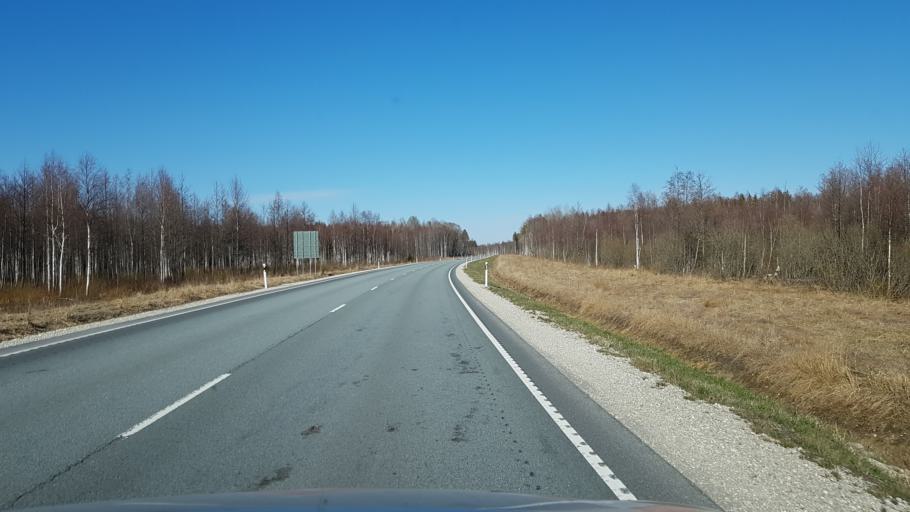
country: EE
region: Jogevamaa
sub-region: Mustvee linn
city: Mustvee
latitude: 58.8553
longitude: 26.9171
